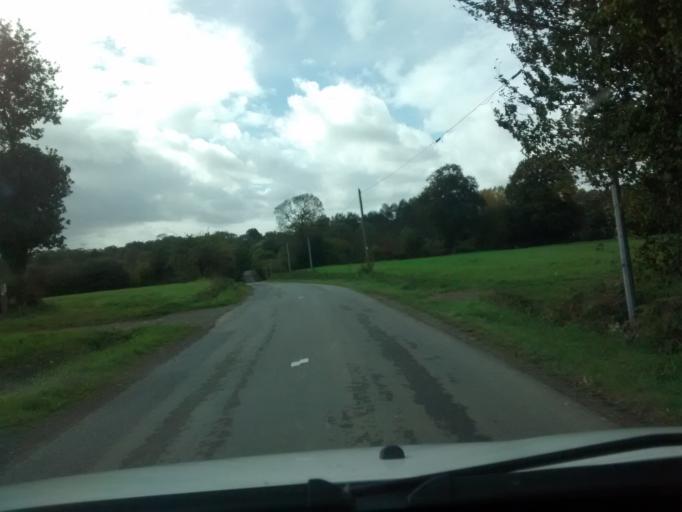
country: FR
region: Brittany
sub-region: Departement d'Ille-et-Vilaine
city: Chateaubourg
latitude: 48.1328
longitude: -1.3959
